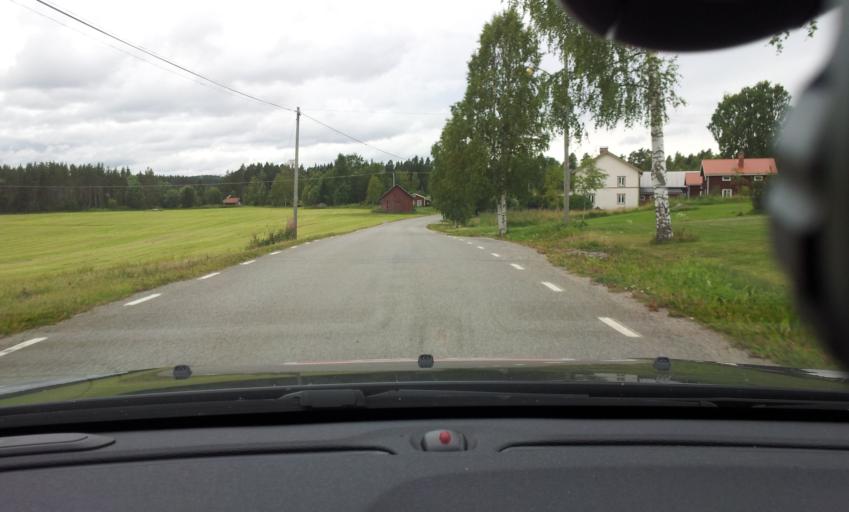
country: SE
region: Jaemtland
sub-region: OEstersunds Kommun
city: Brunflo
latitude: 62.9628
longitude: 15.1287
